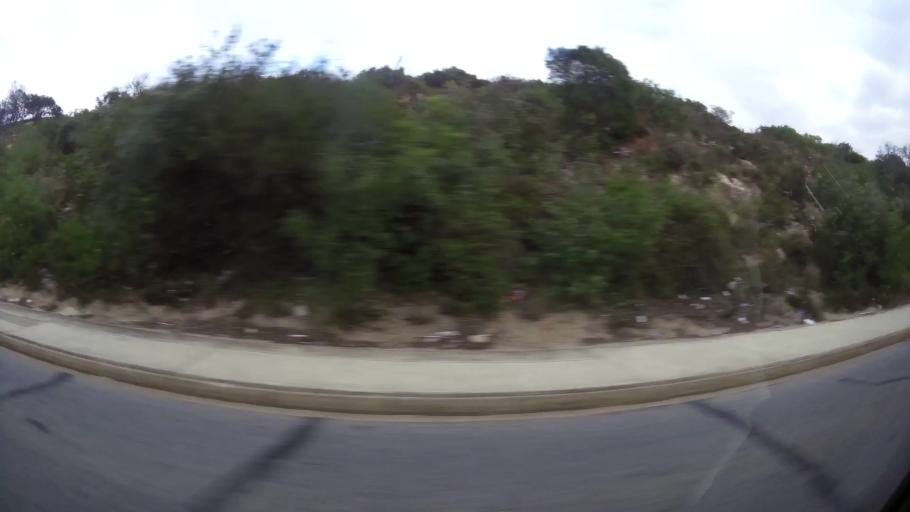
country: ZA
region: Eastern Cape
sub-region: Nelson Mandela Bay Metropolitan Municipality
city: Port Elizabeth
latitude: -33.9546
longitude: 25.5552
